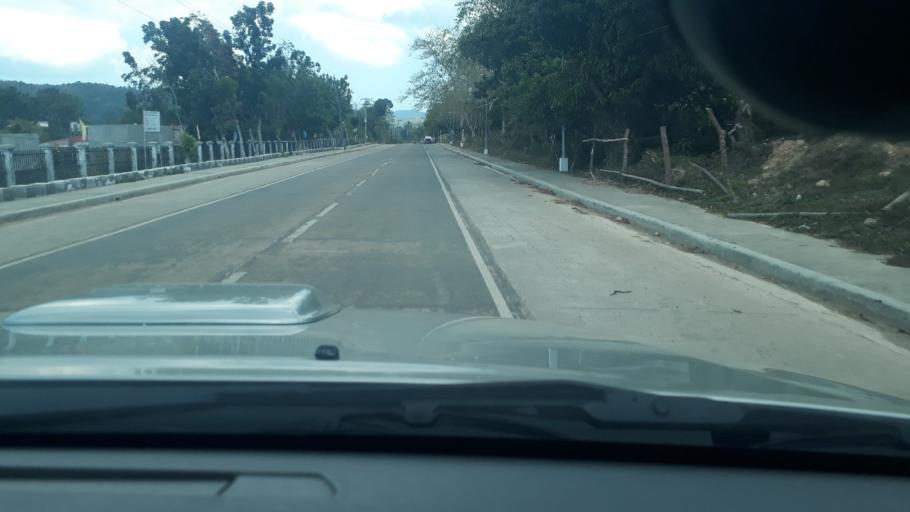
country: PH
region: Mimaropa
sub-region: Province of Palawan
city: Salvacion
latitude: 12.1322
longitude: 119.9372
